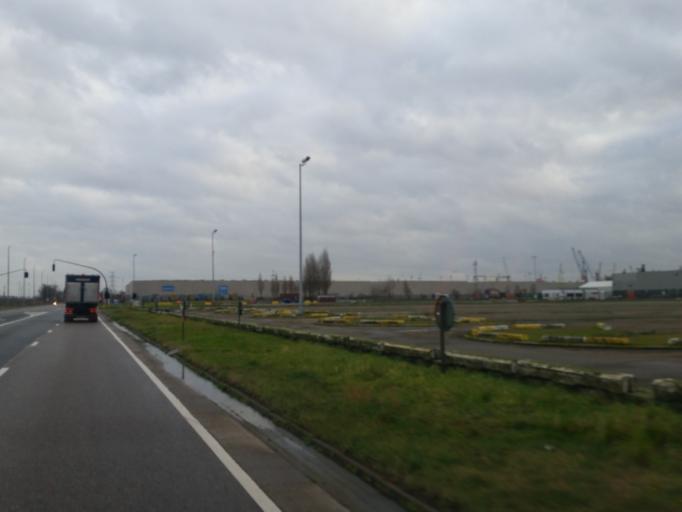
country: BE
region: Flanders
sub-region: Provincie Antwerpen
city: Stabroek
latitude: 51.2906
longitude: 4.3711
